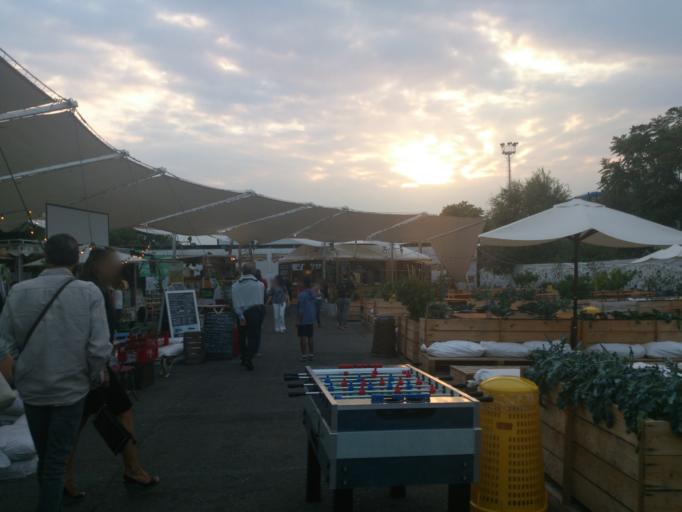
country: IT
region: Lombardy
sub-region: Citta metropolitana di Milano
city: Milano
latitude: 45.4499
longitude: 9.1641
